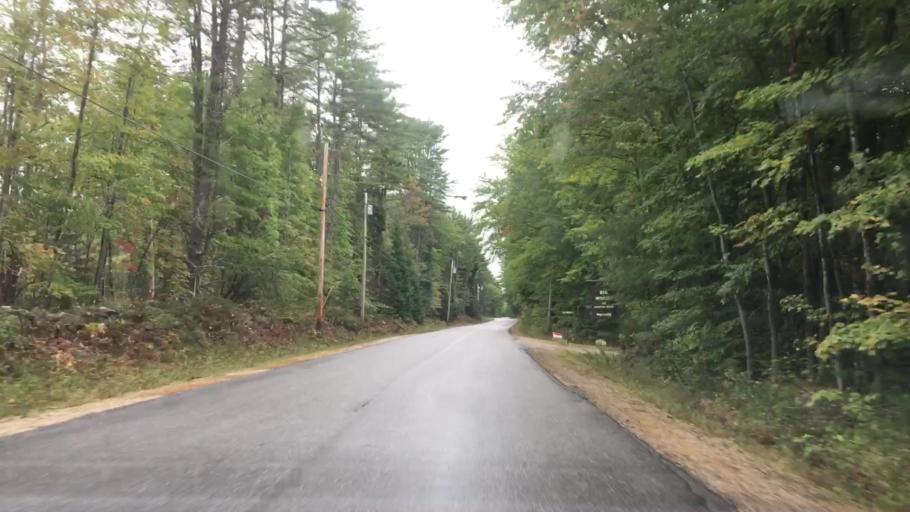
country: US
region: Maine
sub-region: Cumberland County
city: Harrison
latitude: 44.0405
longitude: -70.6095
